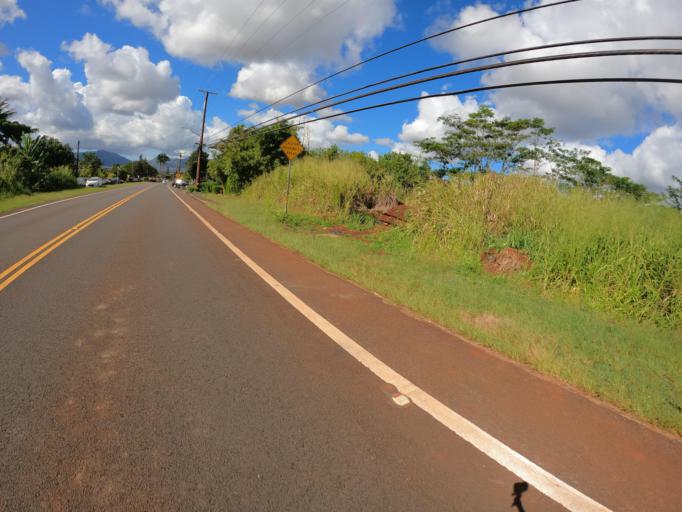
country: US
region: Hawaii
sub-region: Honolulu County
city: Whitmore Village
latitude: 21.5119
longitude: -158.0172
